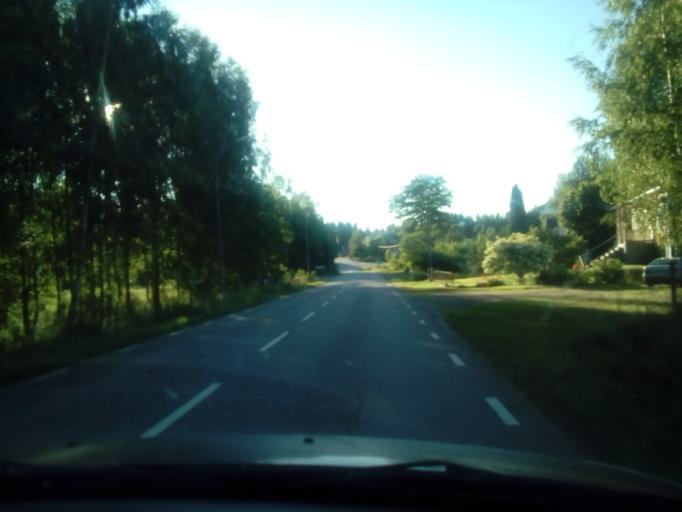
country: SE
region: Kalmar
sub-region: Vasterviks Kommun
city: Ankarsrum
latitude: 57.7885
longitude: 16.1919
